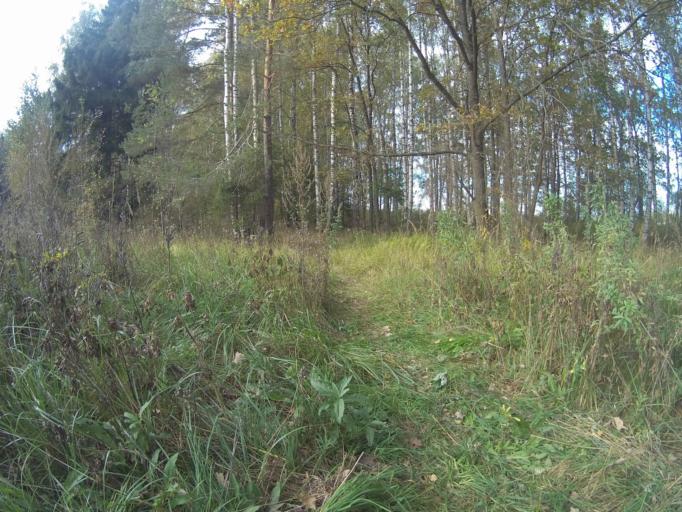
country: RU
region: Vladimir
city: Golovino
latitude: 55.9675
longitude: 40.4407
